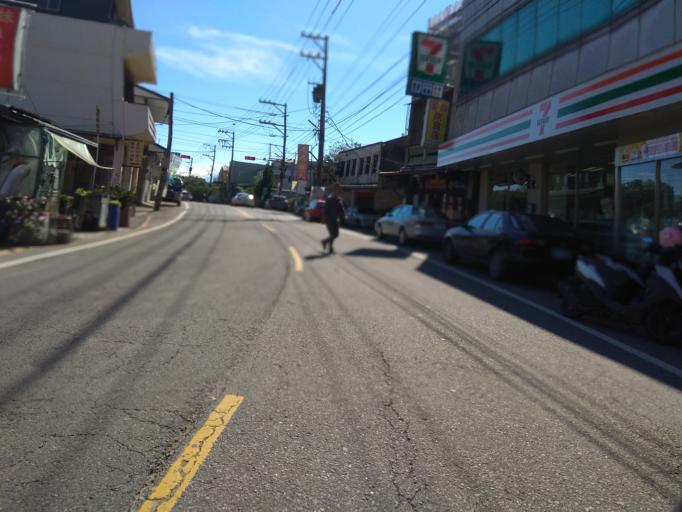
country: TW
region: Taiwan
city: Taoyuan City
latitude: 24.9734
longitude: 121.1392
